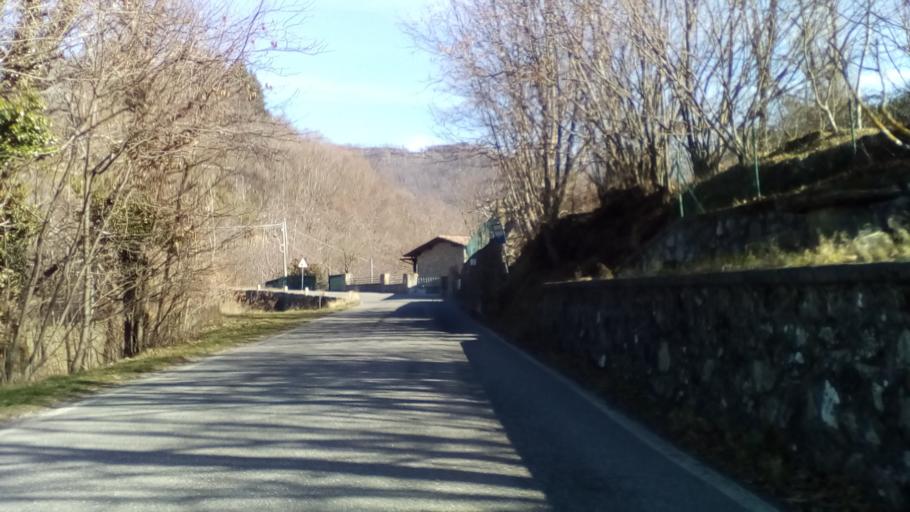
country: IT
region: Tuscany
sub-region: Provincia di Lucca
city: Castiglione di Garfagnana
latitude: 44.1498
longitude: 10.4405
